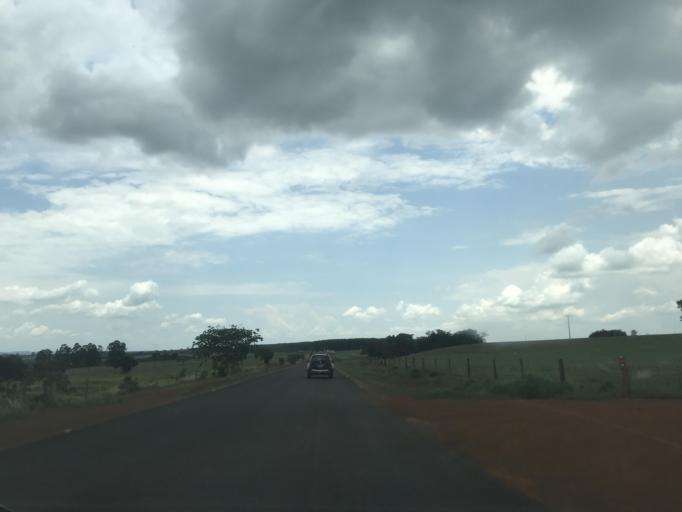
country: BR
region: Goias
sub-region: Vianopolis
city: Vianopolis
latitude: -16.9155
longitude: -48.5550
